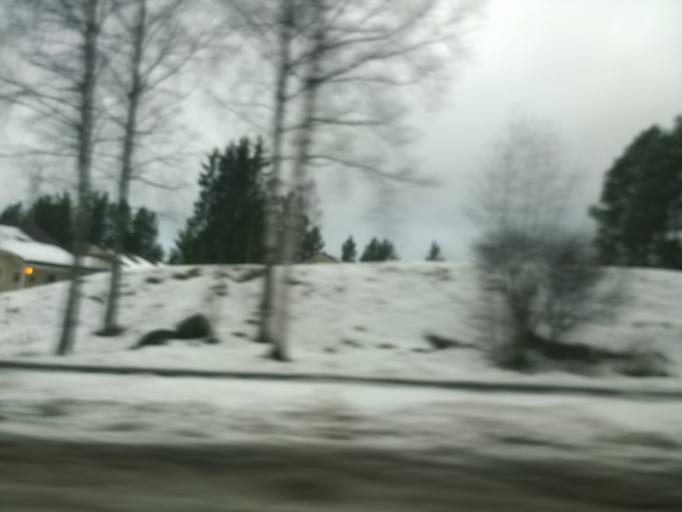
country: FI
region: Pirkanmaa
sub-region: Tampere
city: Lempaeaelae
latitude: 61.3920
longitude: 23.7775
